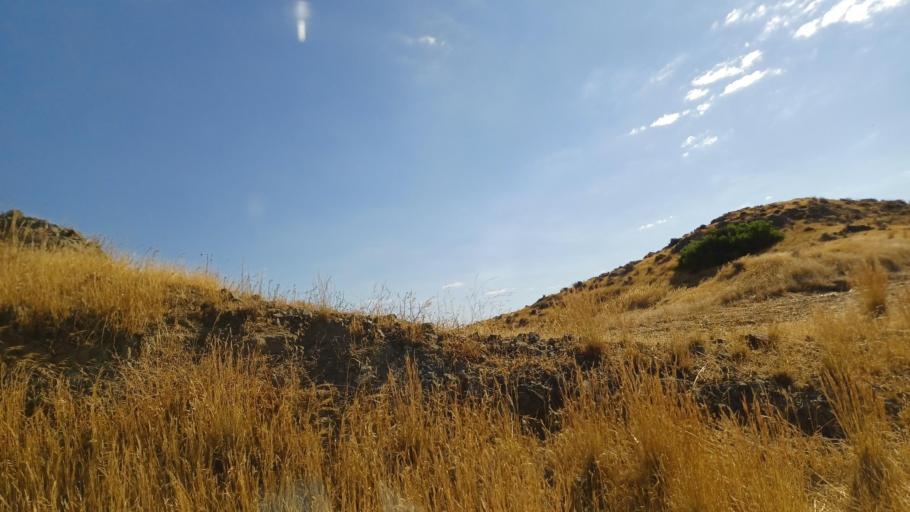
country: CY
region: Larnaka
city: Troulloi
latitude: 35.0041
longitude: 33.5916
